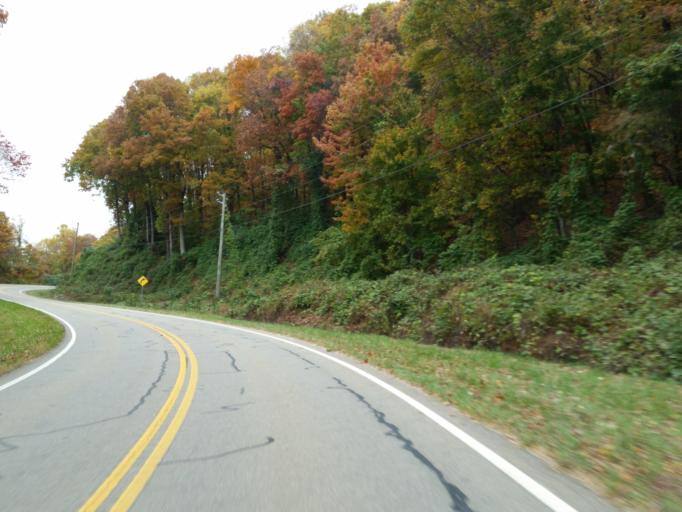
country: US
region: Georgia
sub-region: Pickens County
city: Jasper
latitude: 34.5393
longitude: -84.3710
